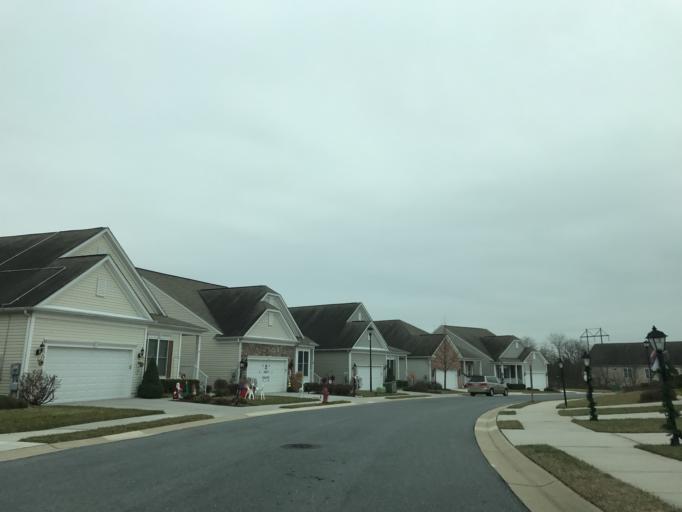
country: US
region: Maryland
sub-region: Carroll County
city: Taneytown
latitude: 39.6436
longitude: -77.1525
